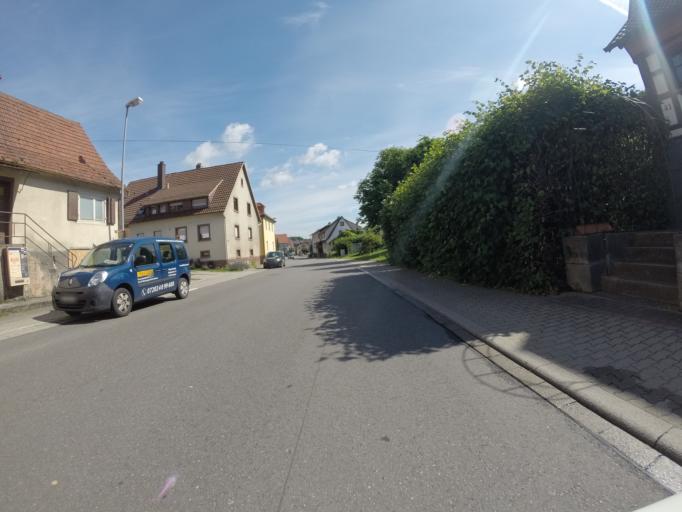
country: DE
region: Baden-Wuerttemberg
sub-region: Karlsruhe Region
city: Ettlingen
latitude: 48.9107
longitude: 8.5046
